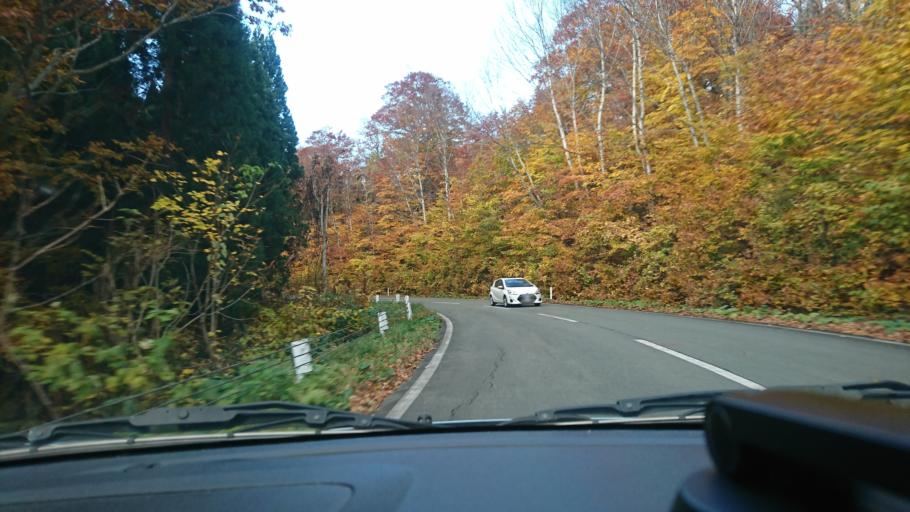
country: JP
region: Akita
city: Yuzawa
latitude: 38.9691
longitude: 140.7130
